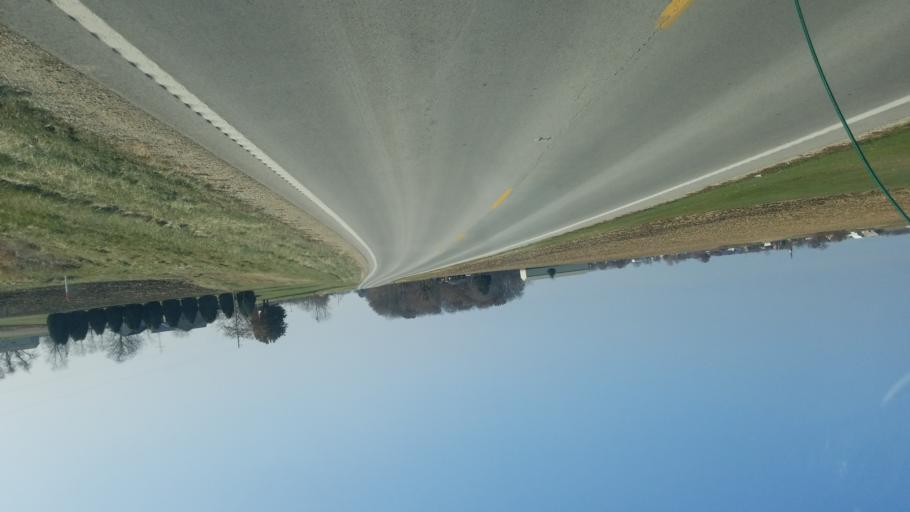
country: US
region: Ohio
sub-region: Mercer County
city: Fort Recovery
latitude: 40.4213
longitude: -84.7525
